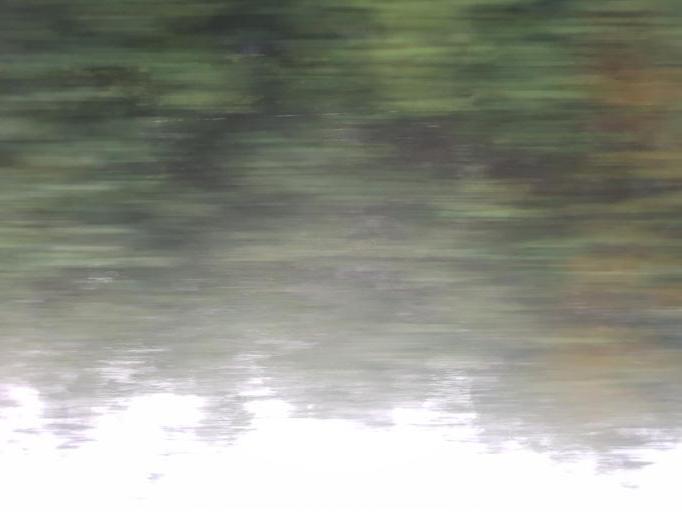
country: NO
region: Sor-Trondelag
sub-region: Trondheim
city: Trondheim
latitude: 63.3663
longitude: 10.3661
